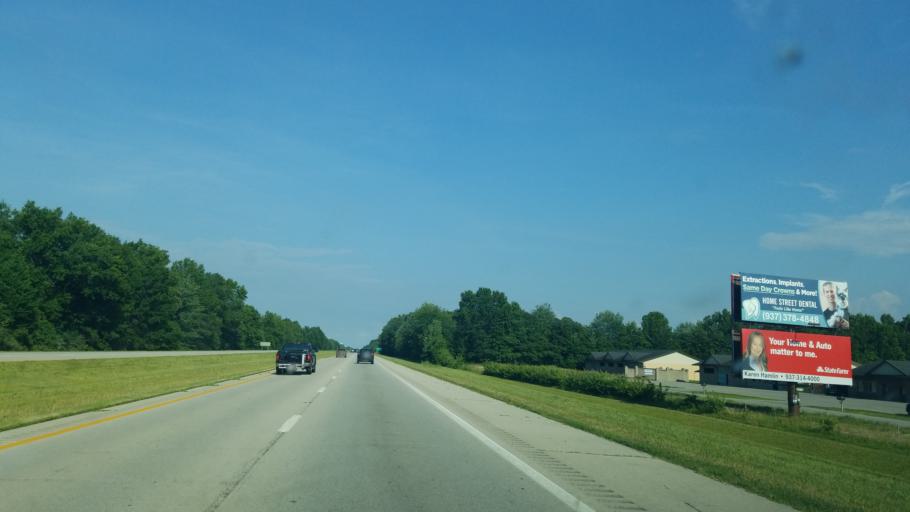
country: US
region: Ohio
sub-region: Brown County
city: Mount Orab
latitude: 39.0548
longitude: -83.9778
